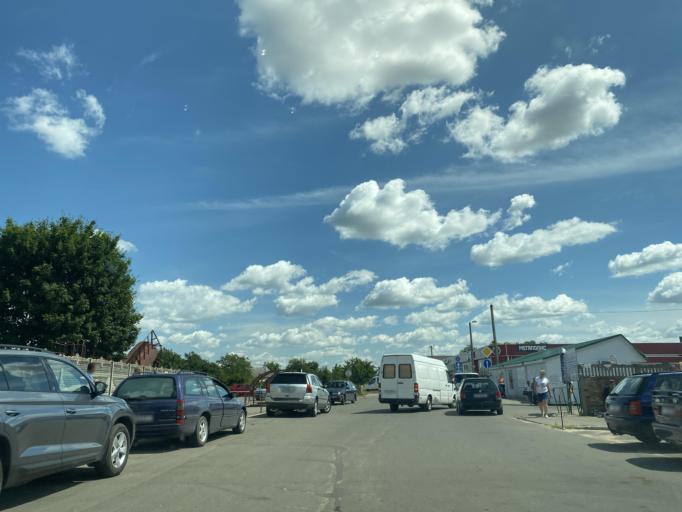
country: BY
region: Brest
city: Ivanava
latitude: 52.1473
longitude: 25.5428
